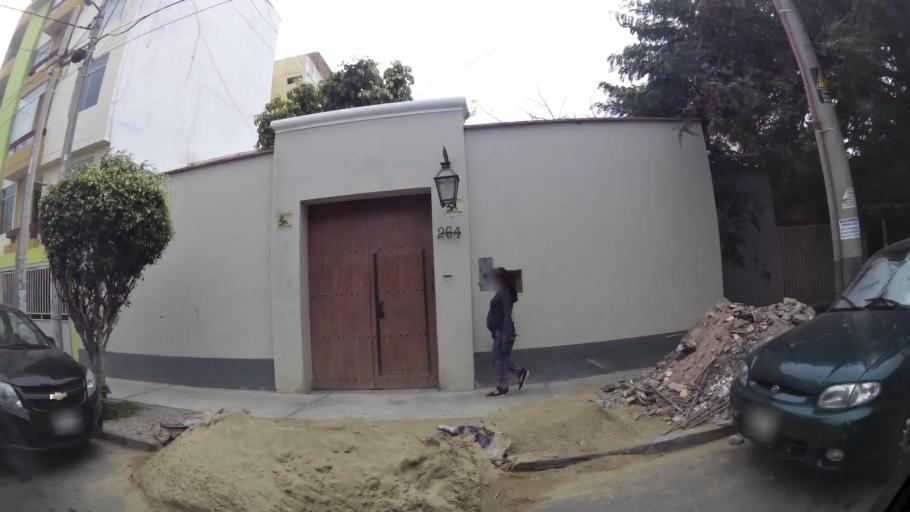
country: PE
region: La Libertad
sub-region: Provincia de Trujillo
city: Buenos Aires
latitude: -8.1342
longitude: -79.0424
